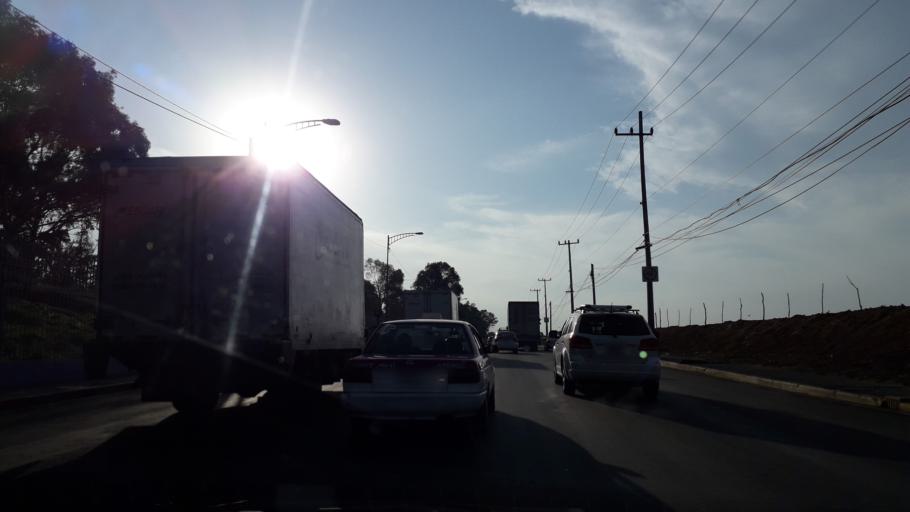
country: MX
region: Mexico City
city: Iztapalapa
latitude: 19.3668
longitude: -99.0408
